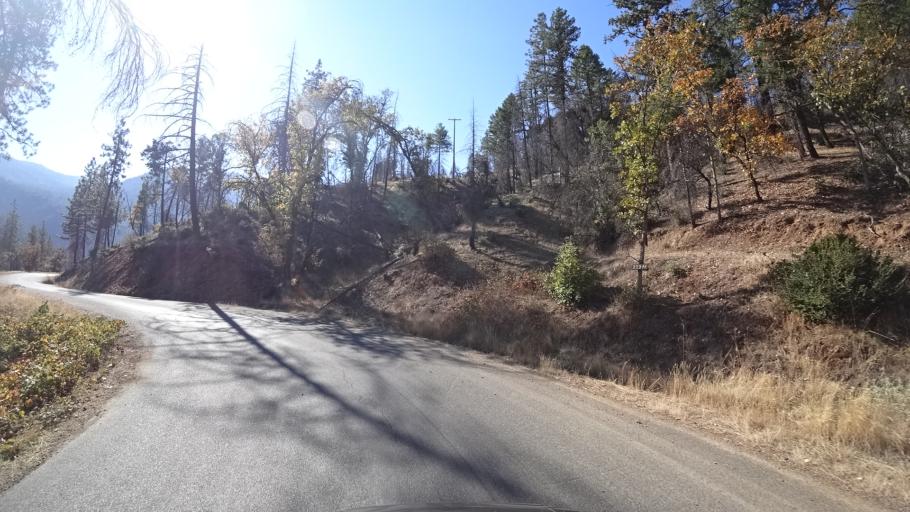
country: US
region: California
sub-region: Siskiyou County
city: Happy Camp
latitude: 41.7183
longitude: -123.0221
